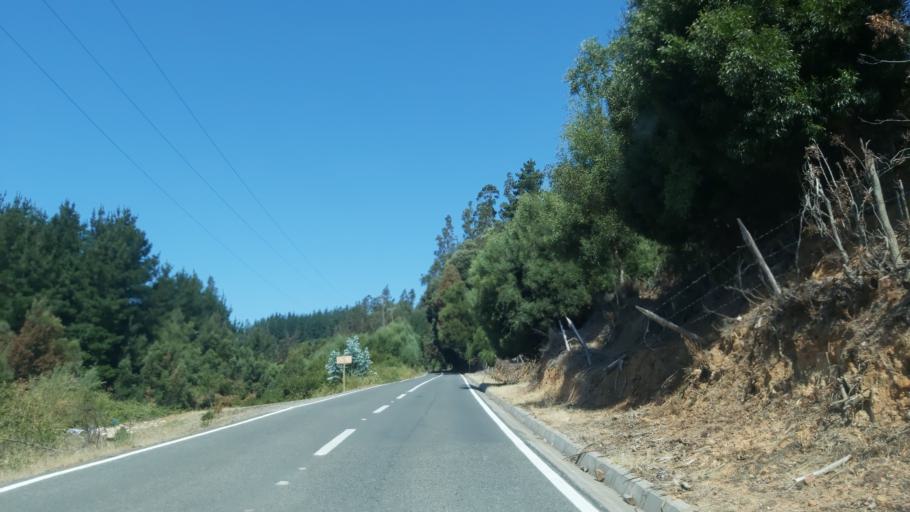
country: CL
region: Biobio
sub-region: Provincia de Concepcion
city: Tome
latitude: -36.5539
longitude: -72.8763
